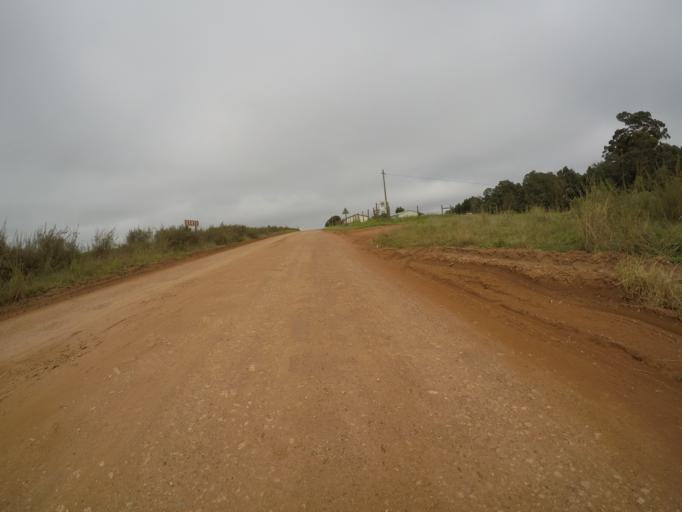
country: ZA
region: Eastern Cape
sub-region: Cacadu District Municipality
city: Kareedouw
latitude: -34.0156
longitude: 24.2382
